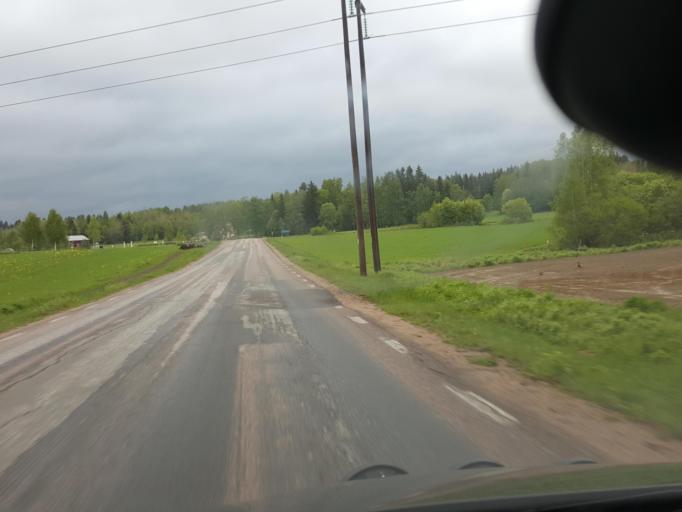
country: SE
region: Gaevleborg
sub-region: Ljusdals Kommun
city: Ljusdal
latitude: 61.8125
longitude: 16.1508
